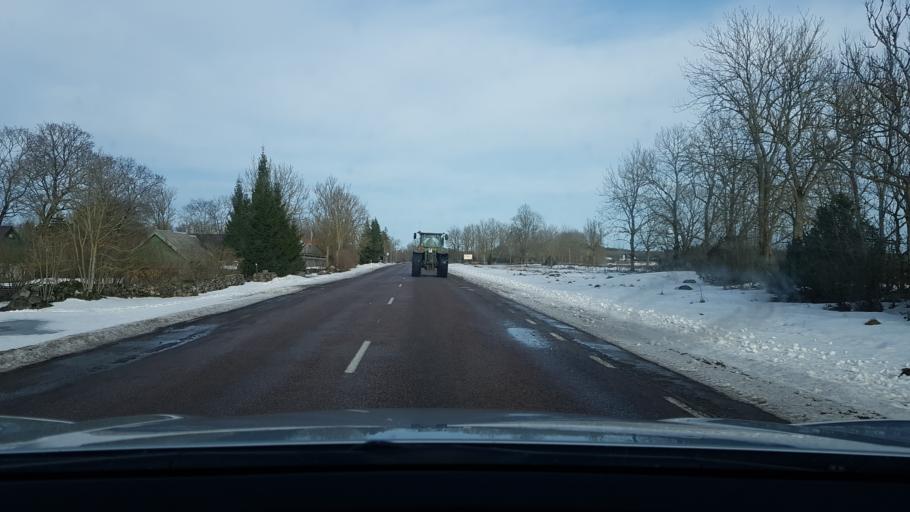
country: EE
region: Saare
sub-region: Kuressaare linn
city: Kuressaare
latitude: 58.3273
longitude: 22.5568
